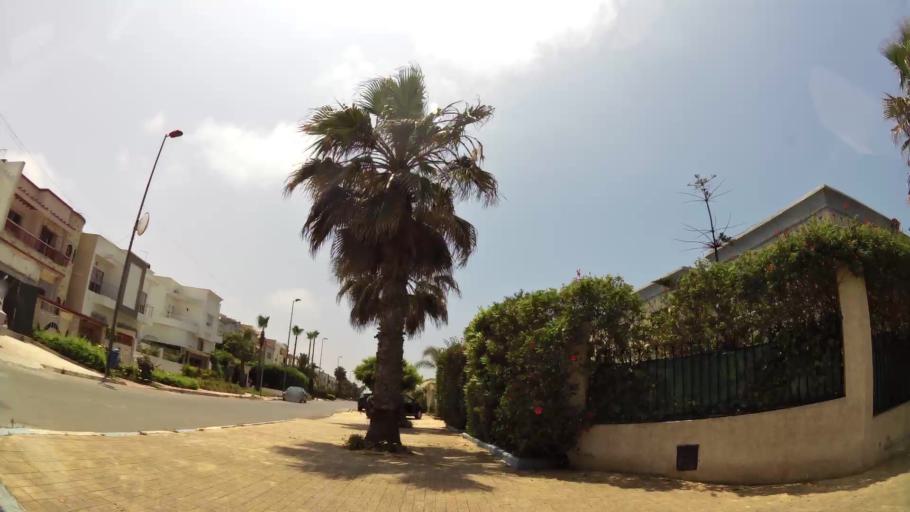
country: MA
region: Rabat-Sale-Zemmour-Zaer
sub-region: Skhirate-Temara
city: Temara
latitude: 33.9699
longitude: -6.9044
